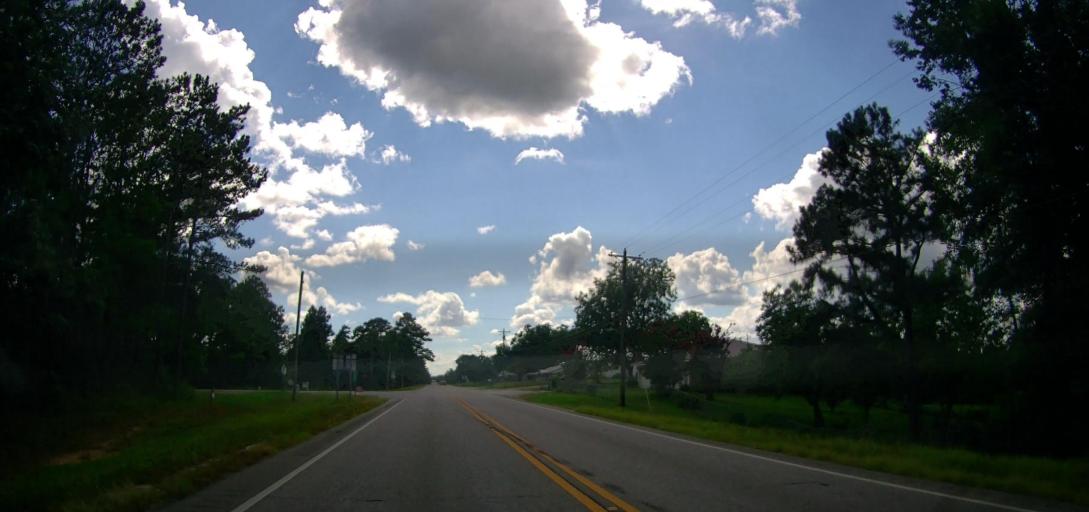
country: US
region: Alabama
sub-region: Macon County
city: Tuskegee
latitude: 32.4675
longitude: -85.5818
